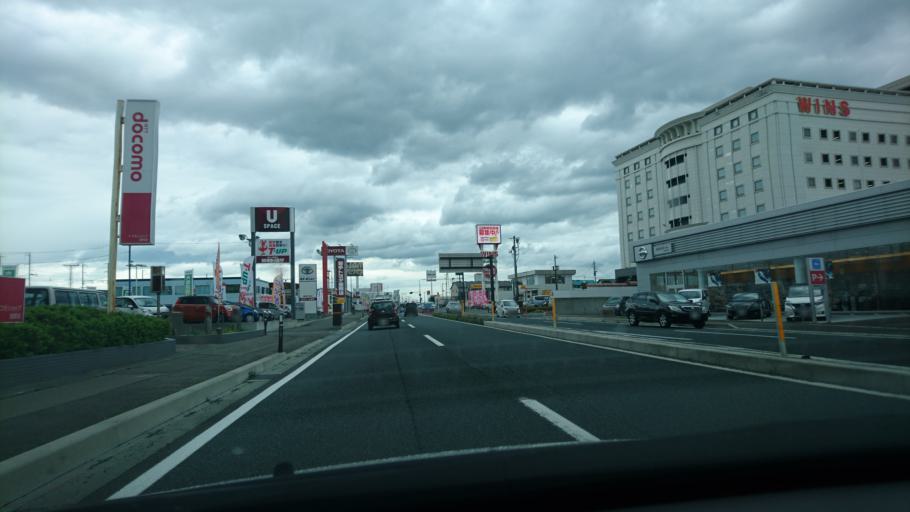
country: JP
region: Iwate
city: Morioka-shi
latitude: 39.7296
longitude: 141.1228
